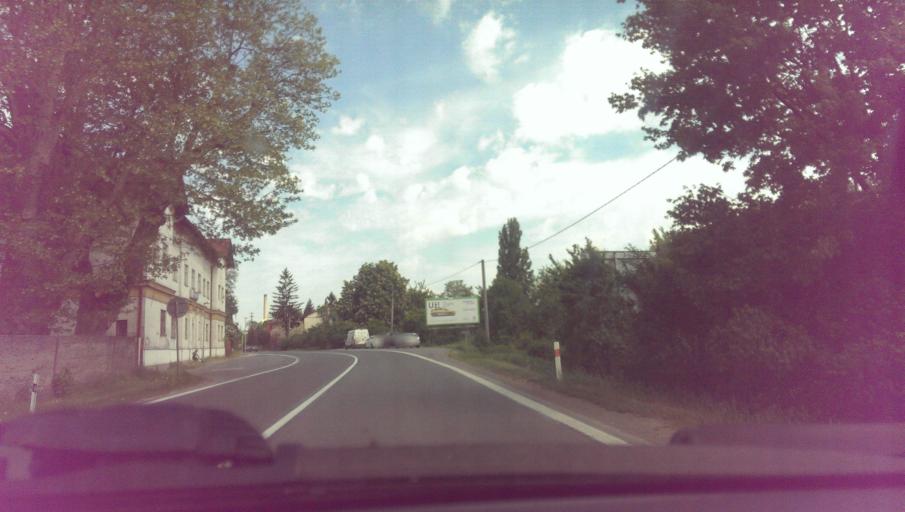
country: CZ
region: Zlin
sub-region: Okres Zlin
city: Napajedla
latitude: 49.1626
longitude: 17.5053
